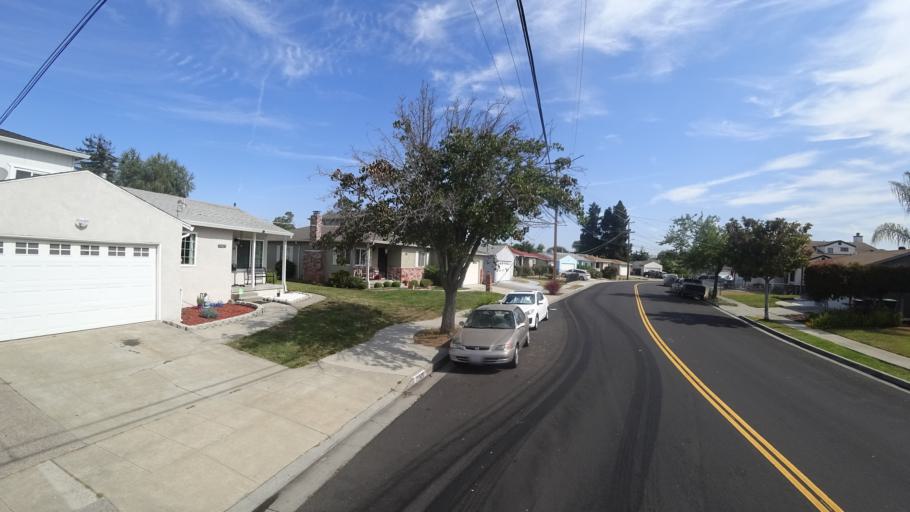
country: US
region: California
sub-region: Alameda County
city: Hayward
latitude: 37.6453
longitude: -122.0908
